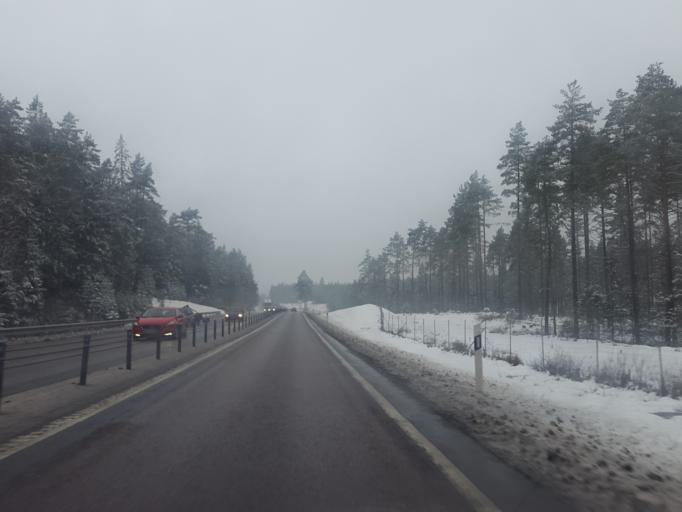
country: SE
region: Joenkoeping
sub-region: Jonkopings Kommun
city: Taberg
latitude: 57.7579
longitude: 13.9994
